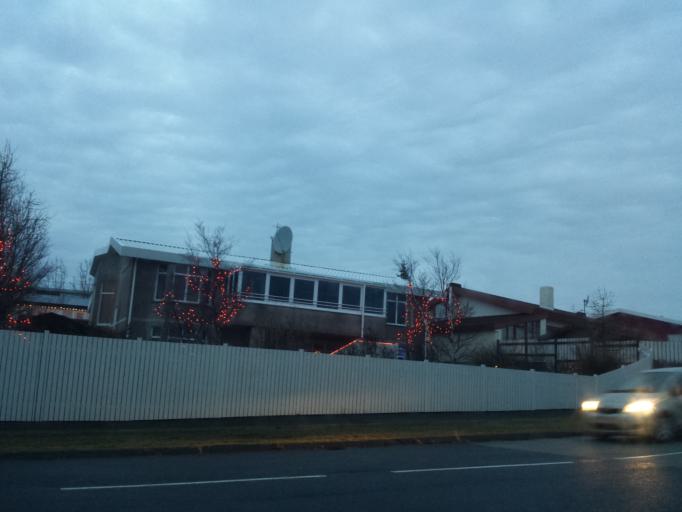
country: IS
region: Capital Region
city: Mosfellsbaer
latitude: 64.1351
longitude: -21.7737
